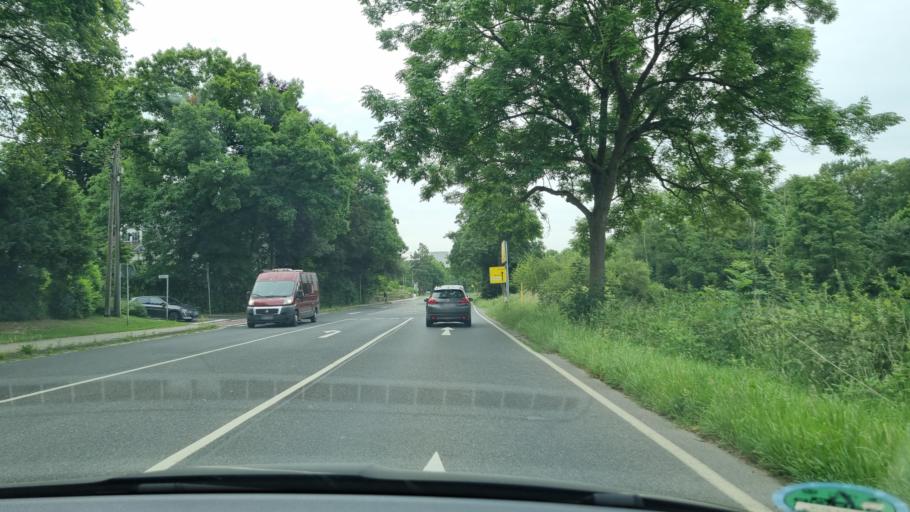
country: DE
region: North Rhine-Westphalia
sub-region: Regierungsbezirk Dusseldorf
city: Voerde
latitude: 51.5982
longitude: 6.6647
